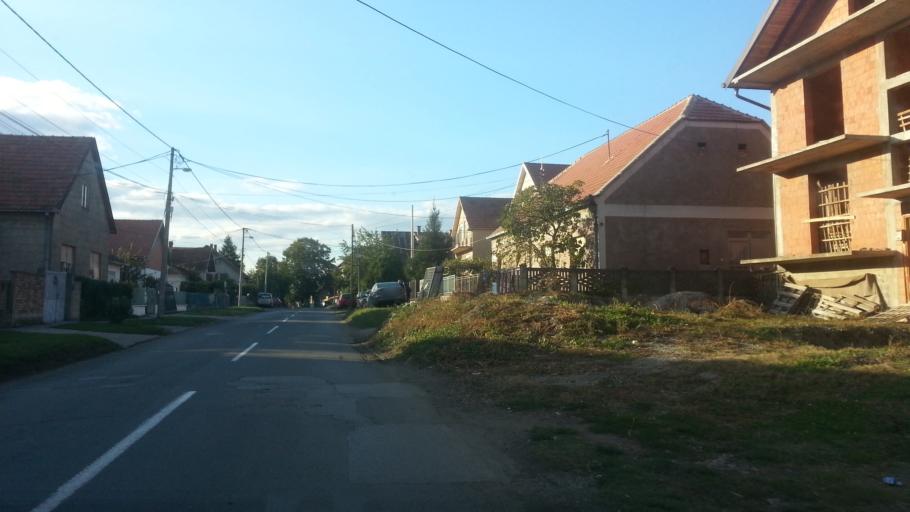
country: RS
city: Novi Banovci
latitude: 44.9097
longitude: 20.2853
